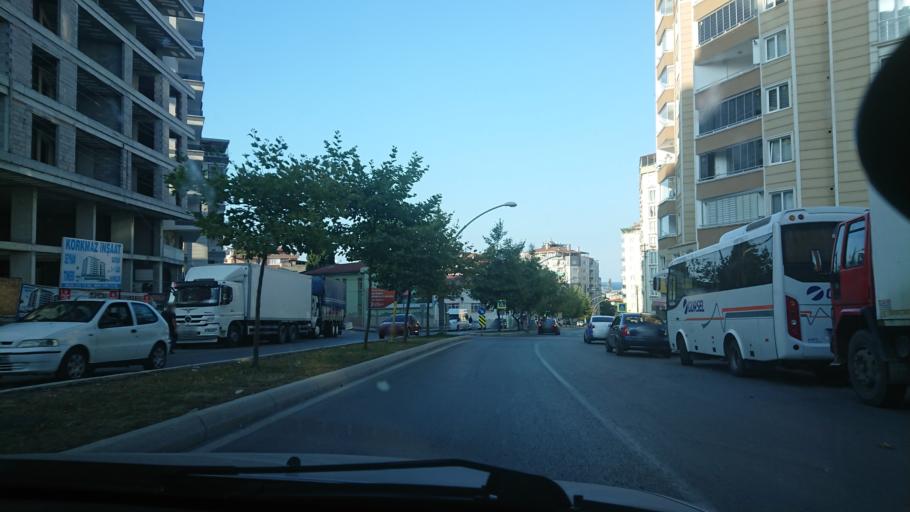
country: TR
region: Samsun
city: Samsun
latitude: 41.3008
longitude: 36.3257
